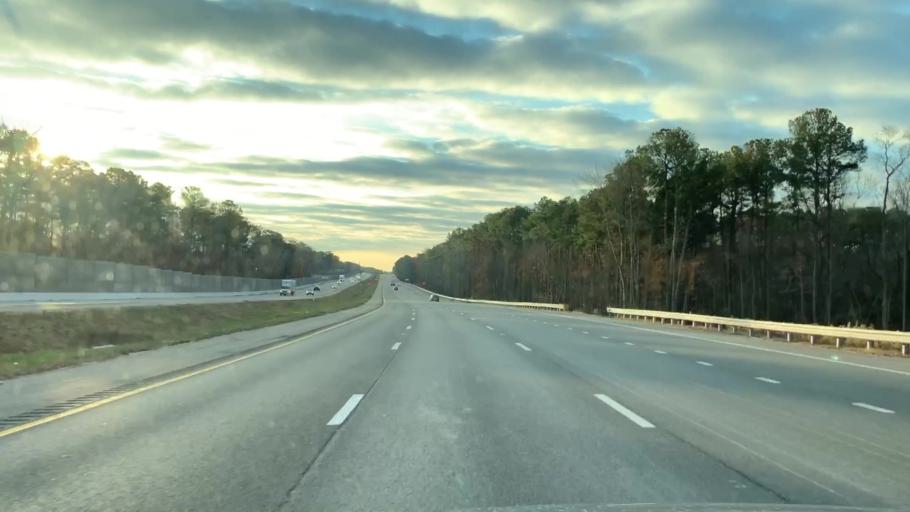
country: US
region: Virginia
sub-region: York County
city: Yorktown
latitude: 37.1708
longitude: -76.5501
